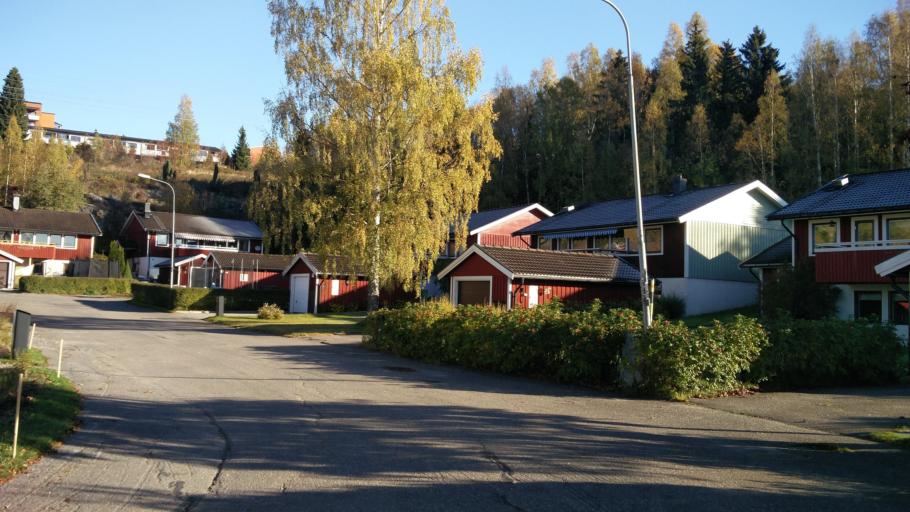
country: SE
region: Vaesternorrland
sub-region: Sundsvalls Kommun
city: Sundsvall
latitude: 62.4066
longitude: 17.2641
